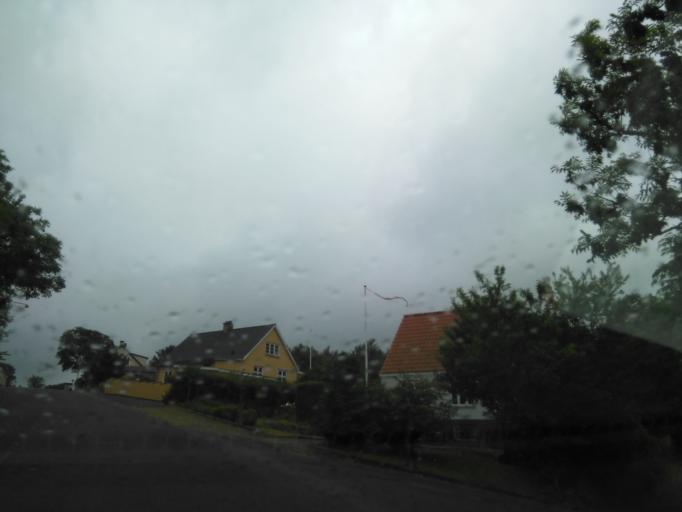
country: DK
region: Capital Region
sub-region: Bornholm Kommune
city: Ronne
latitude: 55.2456
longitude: 14.7411
